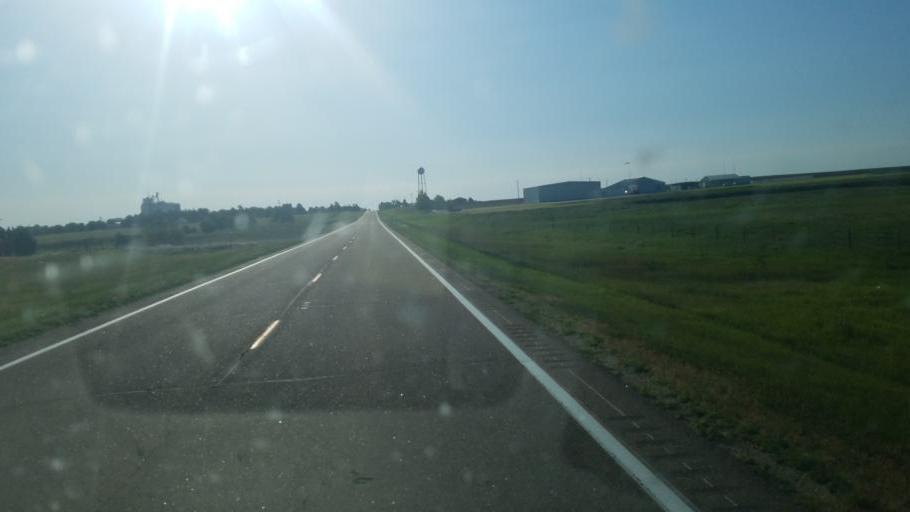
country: US
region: Kansas
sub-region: Edwards County
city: Kinsley
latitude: 38.1897
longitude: -99.5374
